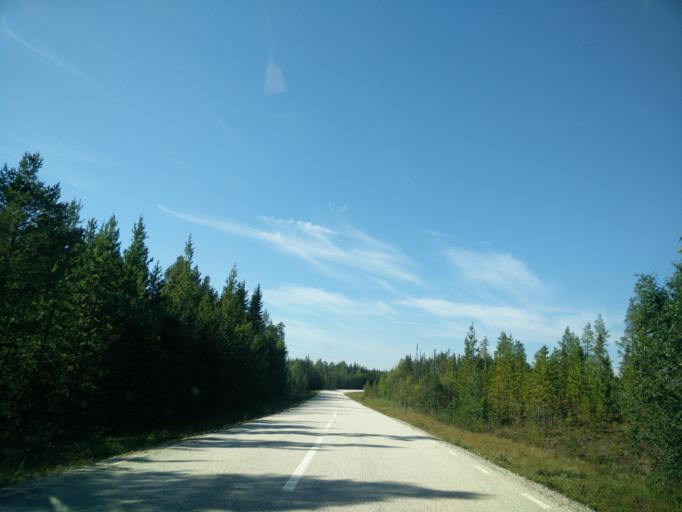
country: SE
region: Jaemtland
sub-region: Are Kommun
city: Jarpen
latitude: 62.8160
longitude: 13.5156
